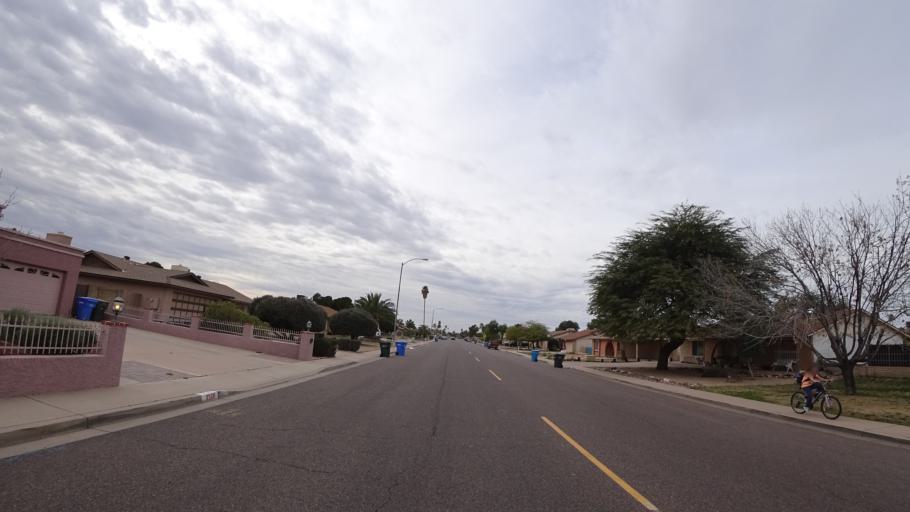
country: US
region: Arizona
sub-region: Maricopa County
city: Peoria
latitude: 33.6473
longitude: -112.1410
